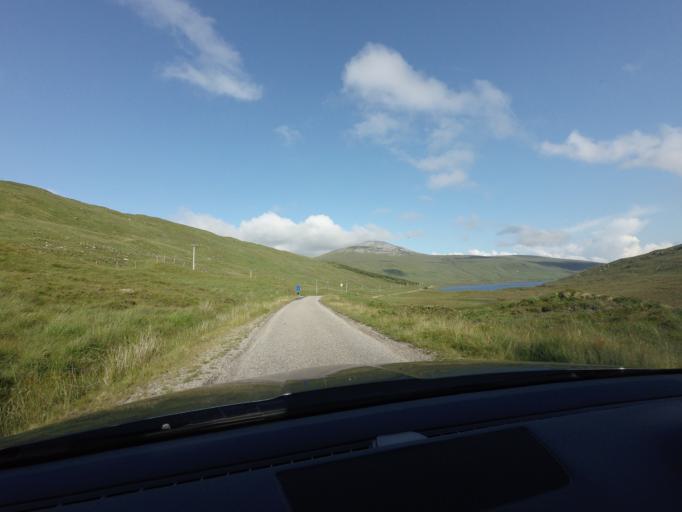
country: GB
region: Scotland
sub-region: Highland
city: Ullapool
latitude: 58.2582
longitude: -4.7808
